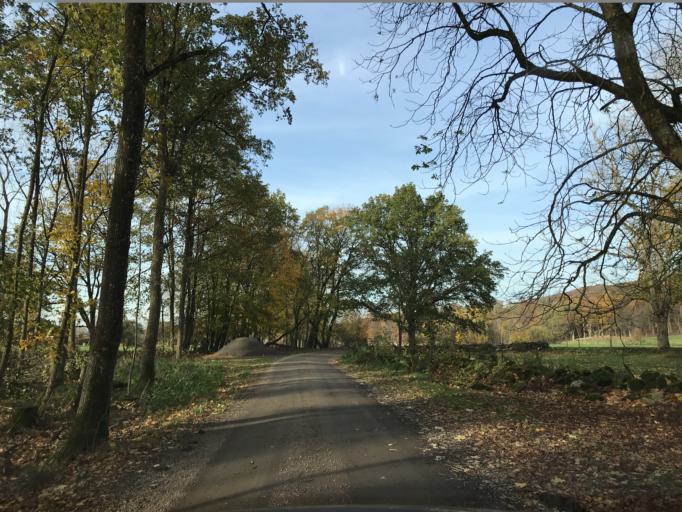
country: SE
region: Skane
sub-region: Bjuvs Kommun
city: Billesholm
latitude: 56.0691
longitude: 13.0154
